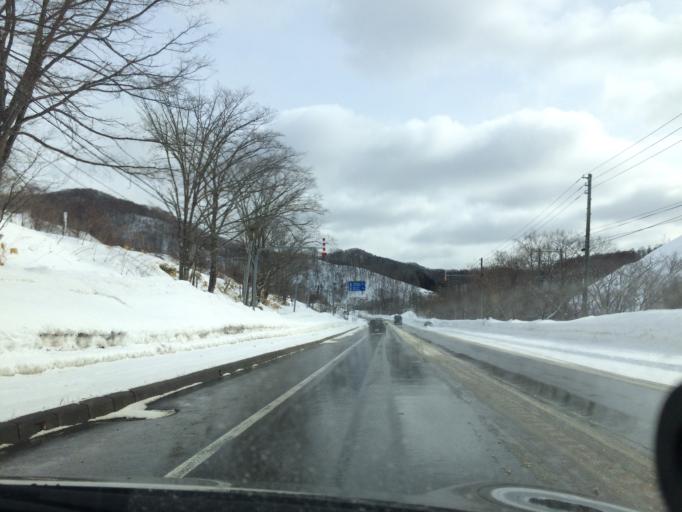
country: JP
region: Hokkaido
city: Iwamizawa
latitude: 43.0196
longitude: 141.9876
